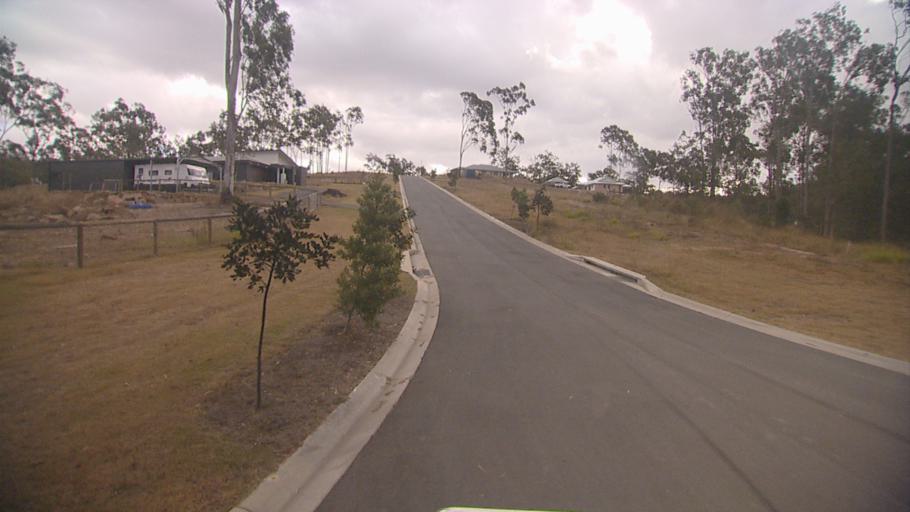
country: AU
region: Queensland
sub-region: Logan
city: Cedar Vale
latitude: -27.8621
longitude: 153.0749
